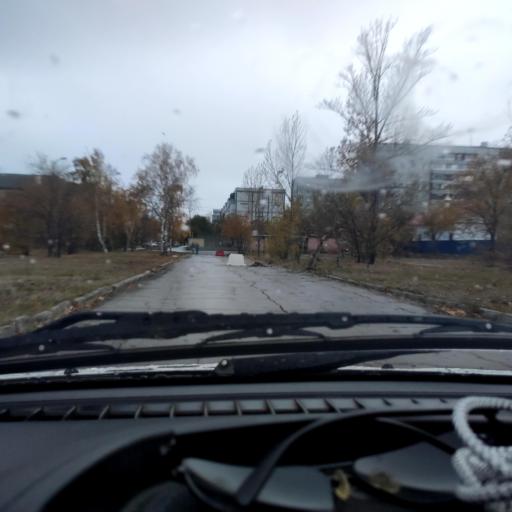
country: RU
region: Samara
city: Zhigulevsk
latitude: 53.4678
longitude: 49.5383
